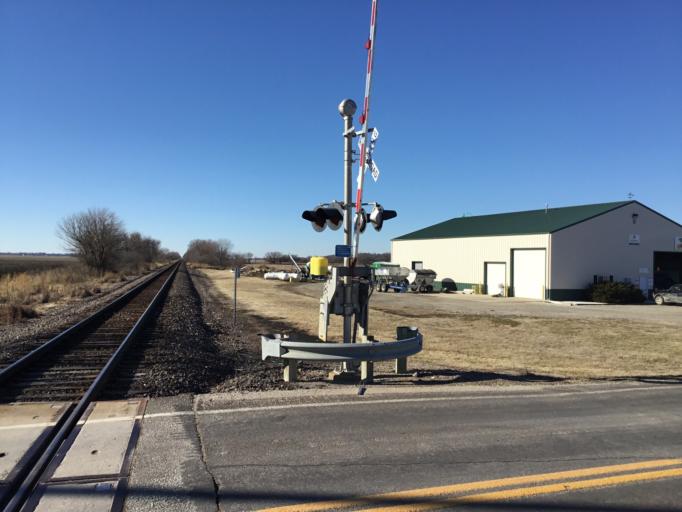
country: US
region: Kansas
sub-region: Shawnee County
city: Silver Lake
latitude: 39.0972
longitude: -95.7978
